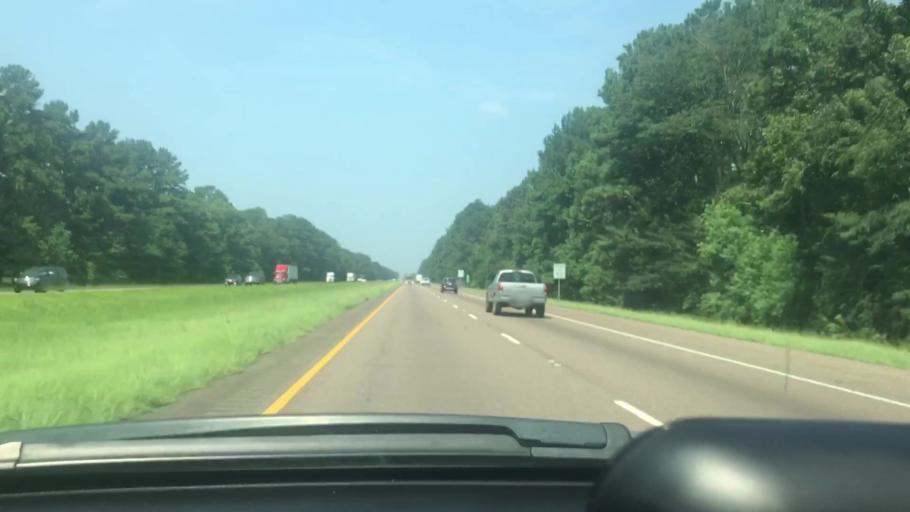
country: US
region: Louisiana
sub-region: Livingston Parish
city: Livingston
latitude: 30.4742
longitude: -90.7604
